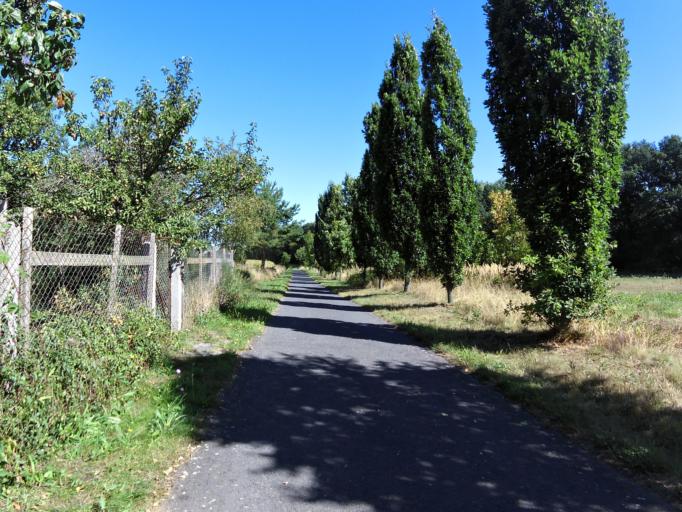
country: DE
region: Saxony-Anhalt
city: Pretzsch
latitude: 51.6880
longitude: 12.8270
